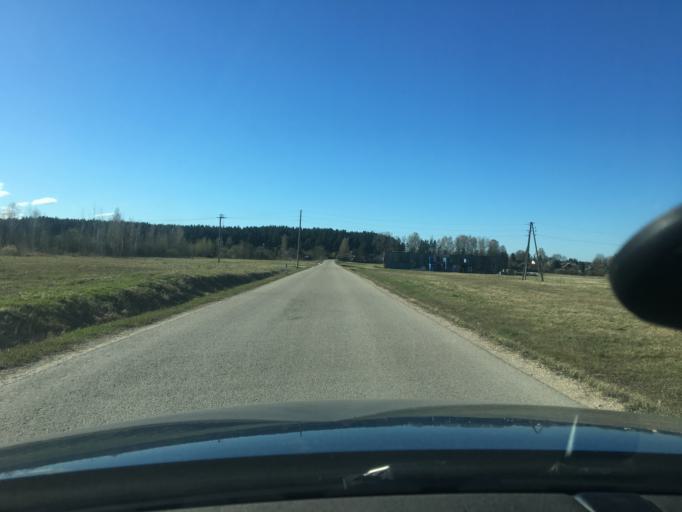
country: LV
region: Kekava
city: Kekava
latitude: 56.8512
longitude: 24.2608
